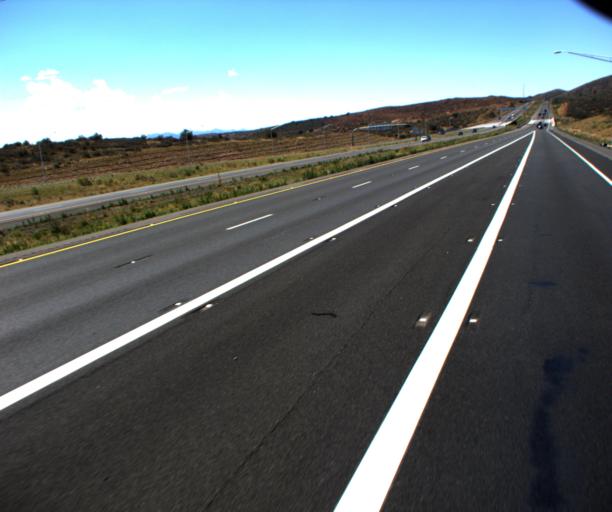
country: US
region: Arizona
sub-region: Yavapai County
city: Cordes Lakes
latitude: 34.3250
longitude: -112.1222
